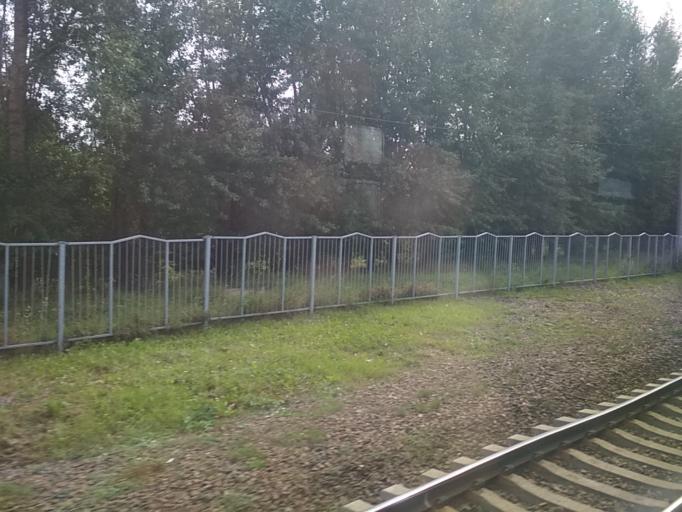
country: BY
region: Minsk
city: Syenitsa
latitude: 53.8535
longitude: 27.5571
